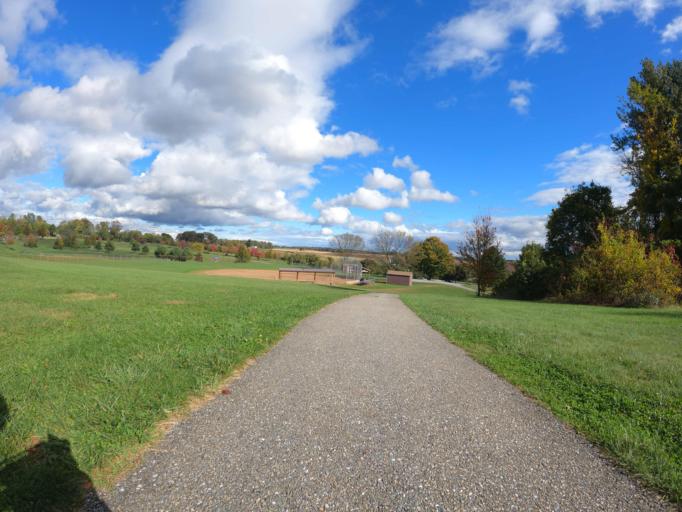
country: US
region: Maryland
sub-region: Carroll County
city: Mount Airy
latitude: 39.3764
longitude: -77.1472
